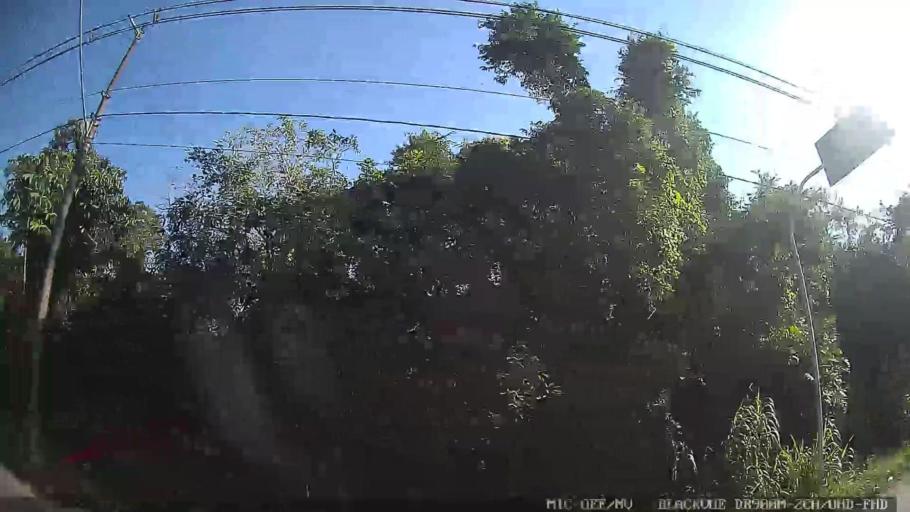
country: BR
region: Sao Paulo
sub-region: Santos
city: Santos
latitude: -23.9027
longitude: -46.3065
